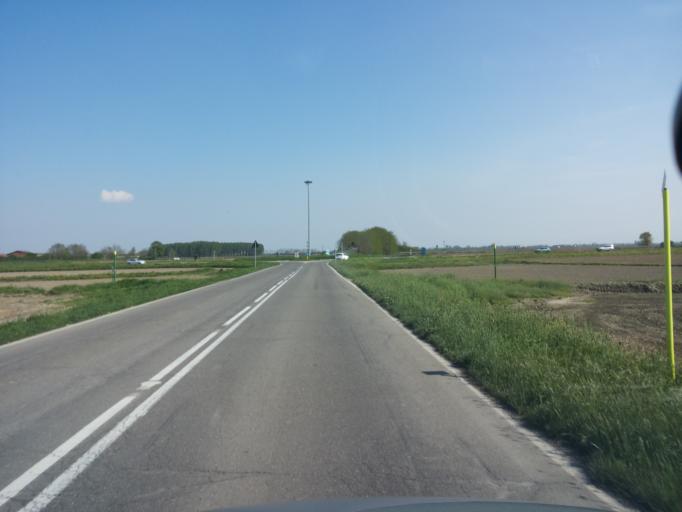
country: IT
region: Lombardy
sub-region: Provincia di Pavia
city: Cozzo
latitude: 45.1877
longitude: 8.6022
